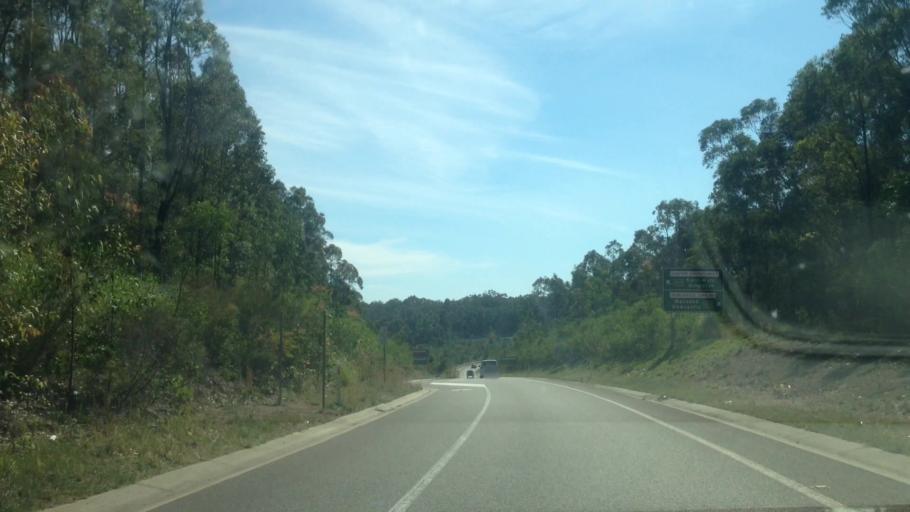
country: AU
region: New South Wales
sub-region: Lake Macquarie Shire
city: Holmesville
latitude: -32.8918
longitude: 151.5959
